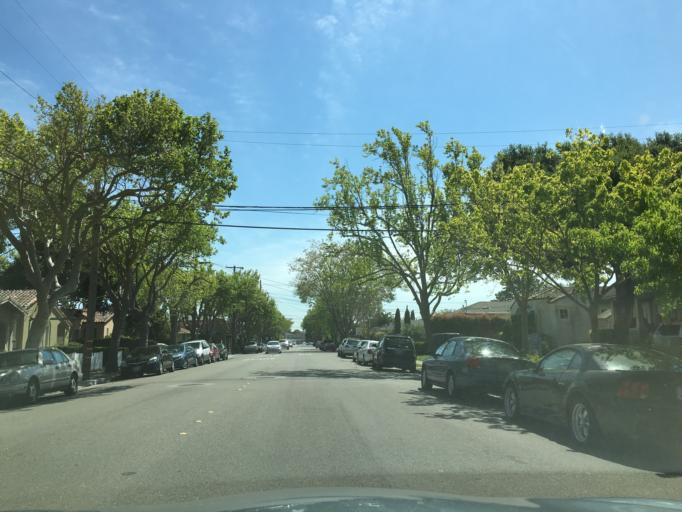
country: US
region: California
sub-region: San Mateo County
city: San Mateo
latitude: 37.5578
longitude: -122.3137
